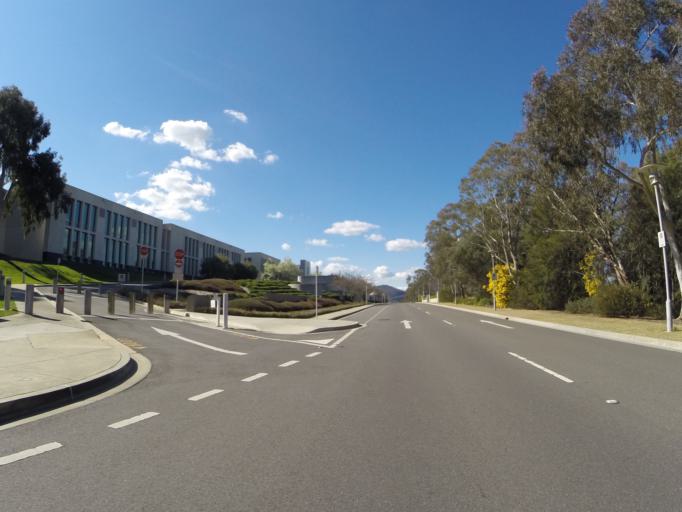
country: AU
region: Australian Capital Territory
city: Forrest
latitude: -35.3103
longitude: 149.1251
